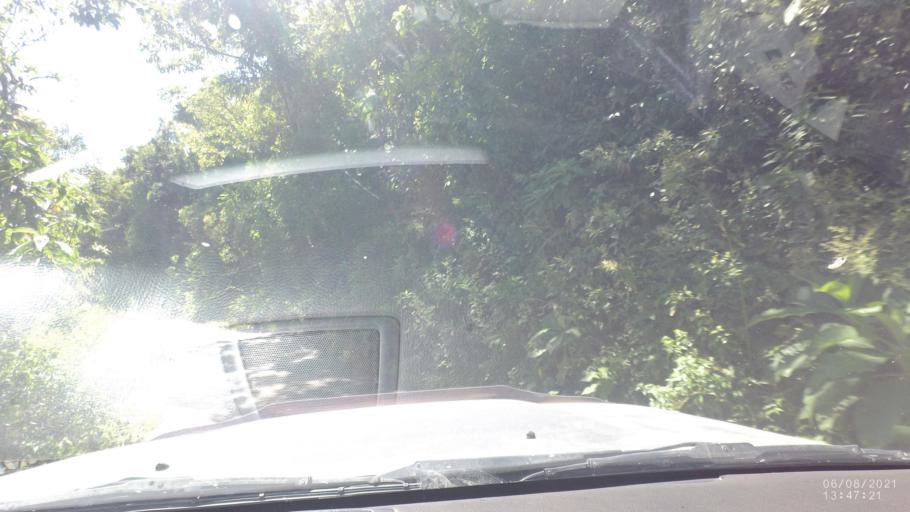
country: BO
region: La Paz
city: Quime
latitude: -16.6679
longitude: -66.7244
